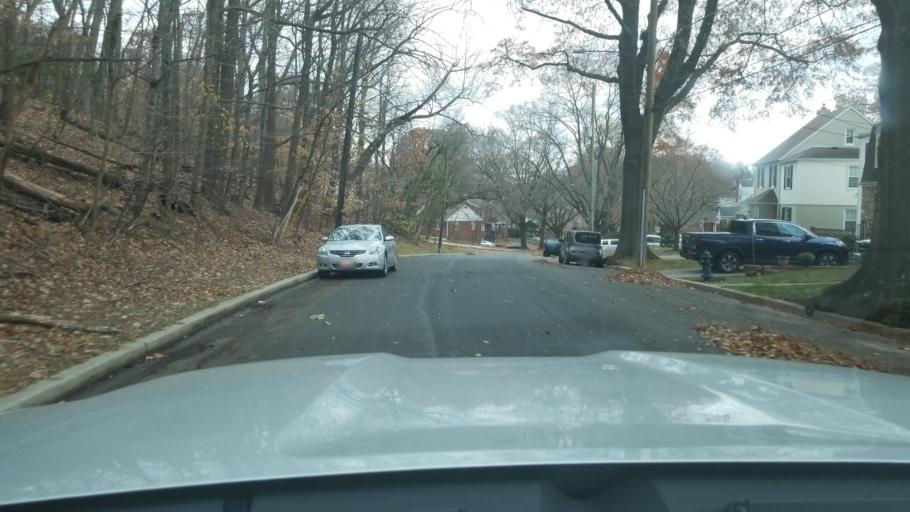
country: US
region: Maryland
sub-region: Prince George's County
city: Coral Hills
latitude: 38.8706
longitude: -76.9497
